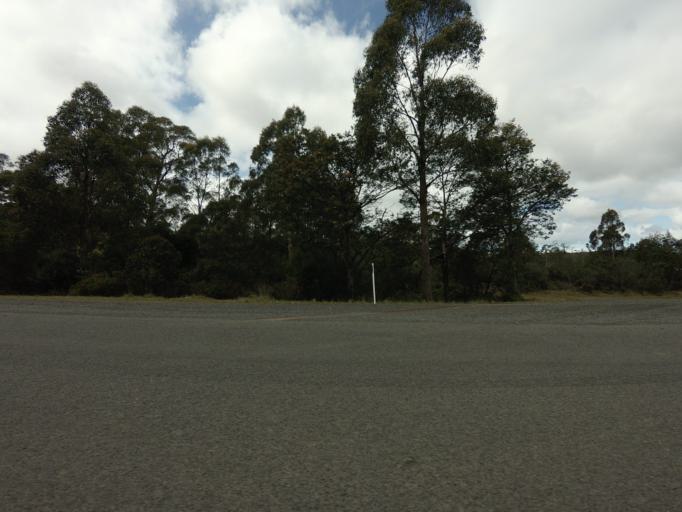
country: AU
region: Tasmania
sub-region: Huon Valley
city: Geeveston
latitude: -43.4203
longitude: 146.9073
